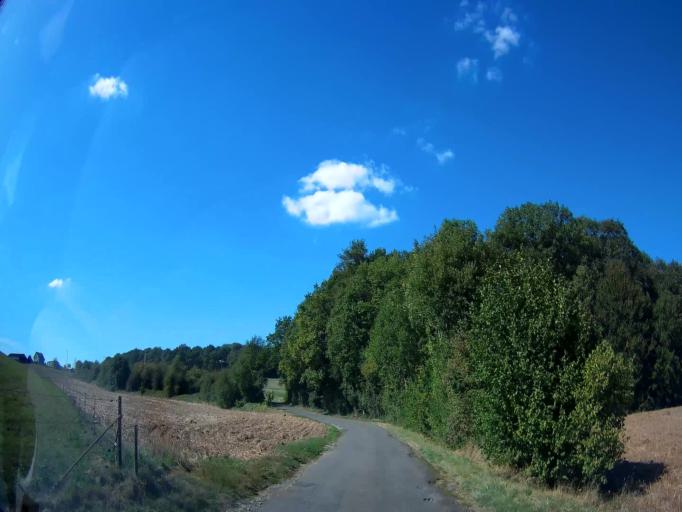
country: BE
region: Wallonia
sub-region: Province de Namur
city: Houyet
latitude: 50.2311
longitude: 4.9819
